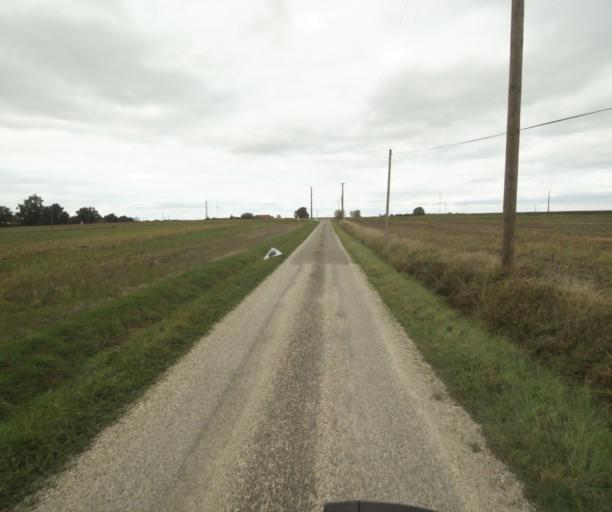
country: FR
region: Midi-Pyrenees
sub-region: Departement du Tarn-et-Garonne
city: Beaumont-de-Lomagne
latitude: 43.8636
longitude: 1.0694
